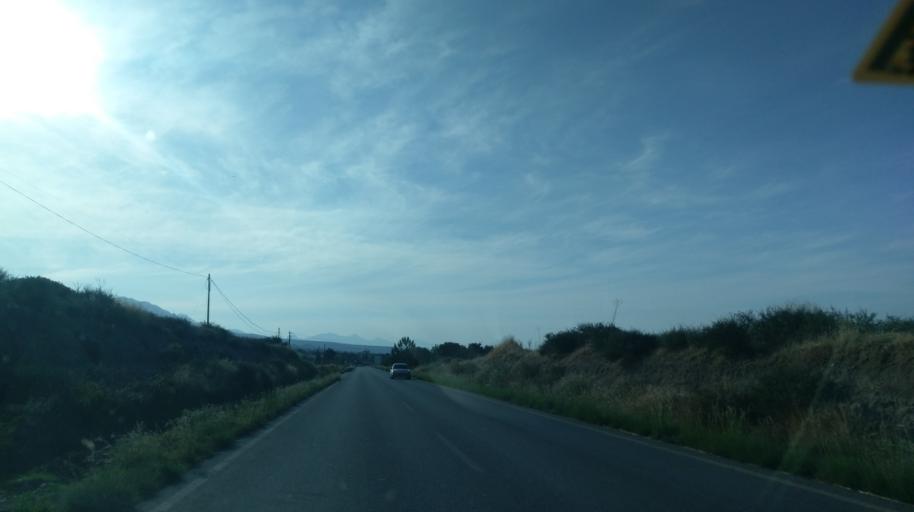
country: CY
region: Ammochostos
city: Lefkonoiko
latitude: 35.3646
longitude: 33.6838
